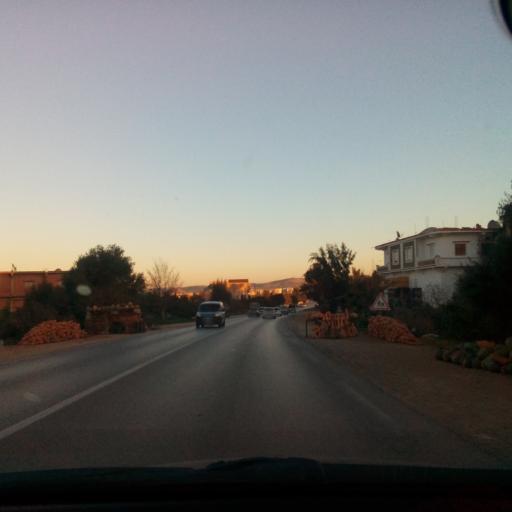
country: DZ
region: Relizane
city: Relizane
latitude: 35.7163
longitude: 0.3344
